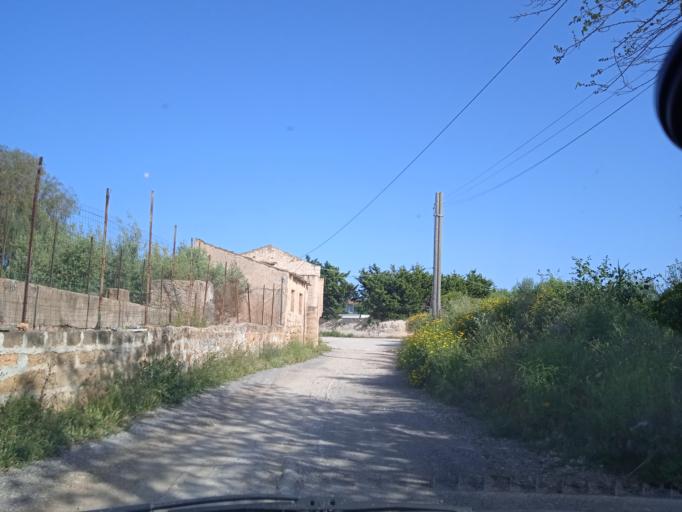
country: IT
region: Sicily
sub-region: Palermo
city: Villabate
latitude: 38.0810
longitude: 13.4536
